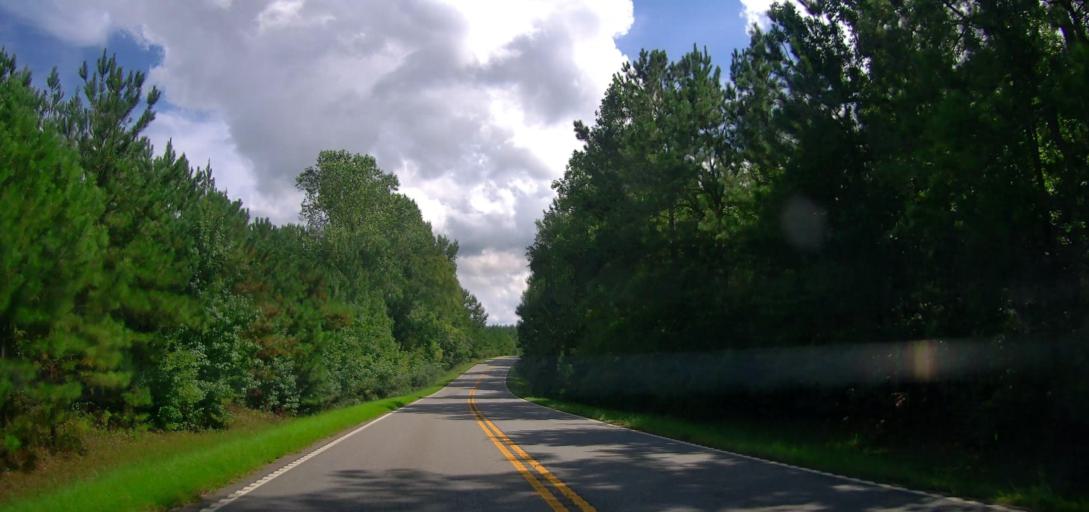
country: US
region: Georgia
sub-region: Talbot County
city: Talbotton
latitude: 32.6557
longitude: -84.5080
